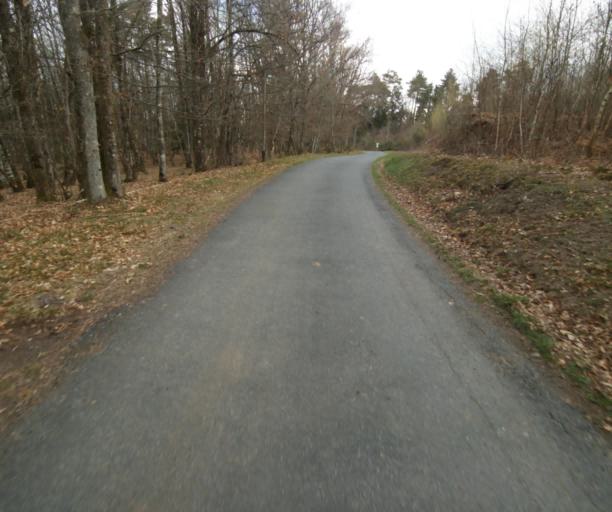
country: FR
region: Limousin
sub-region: Departement de la Correze
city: Correze
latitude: 45.2767
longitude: 1.9509
